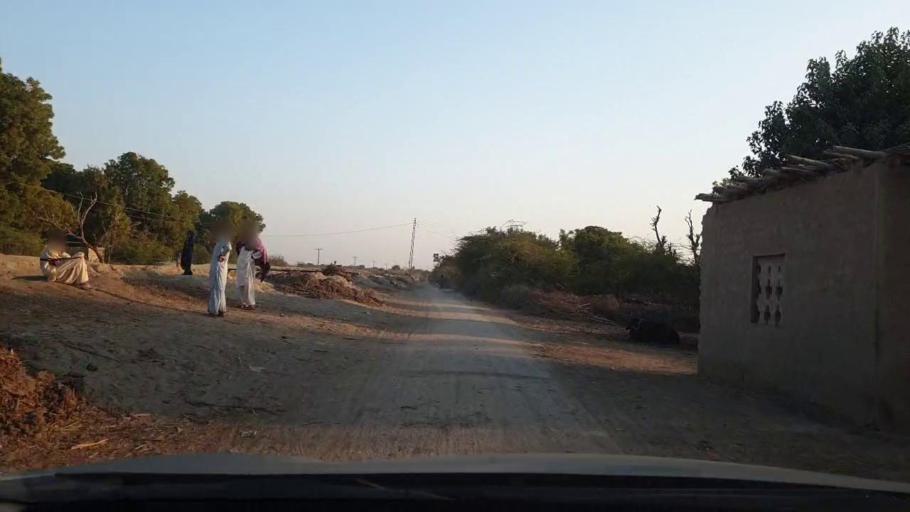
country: PK
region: Sindh
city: Tando Adam
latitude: 25.6836
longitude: 68.7455
